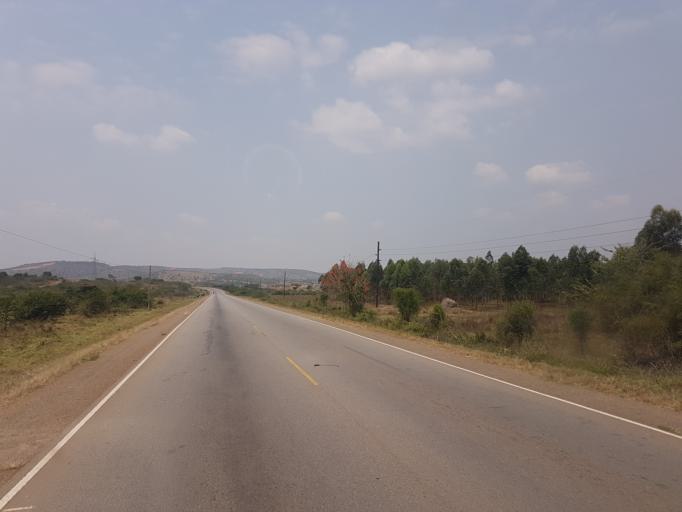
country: UG
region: Western Region
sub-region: Mbarara District
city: Mbarara
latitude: -0.5098
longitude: 30.8341
